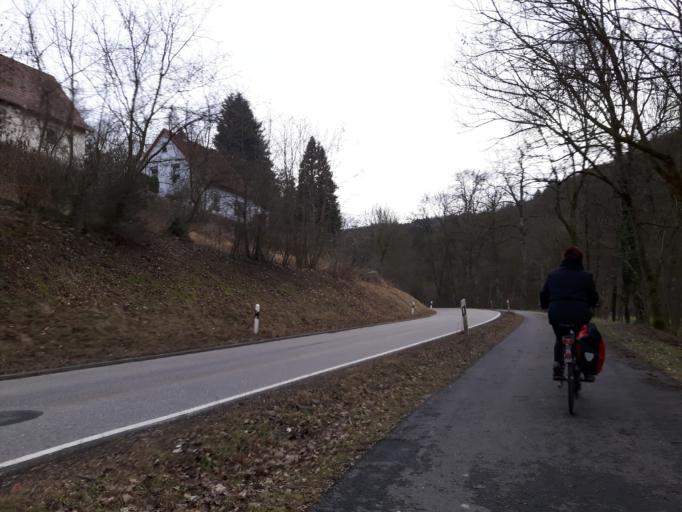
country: DE
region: Baden-Wuerttemberg
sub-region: Regierungsbezirk Stuttgart
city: Zweiflingen
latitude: 49.2461
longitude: 9.4555
